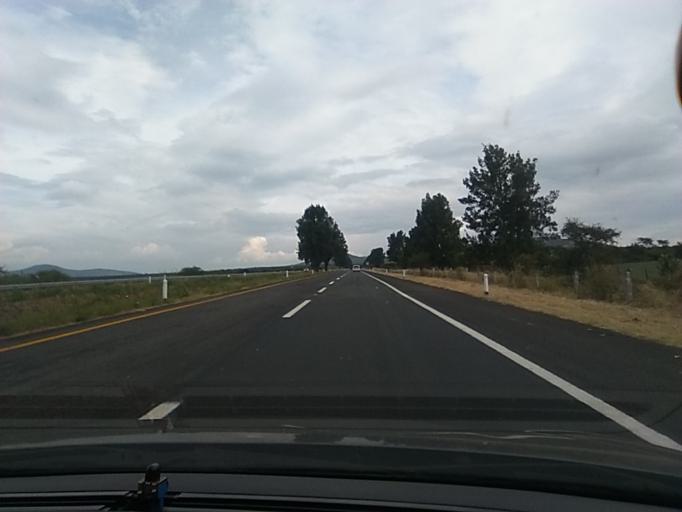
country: MX
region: Michoacan
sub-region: Vista Hermosa
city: La Angostura
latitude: 20.2485
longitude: -102.4136
